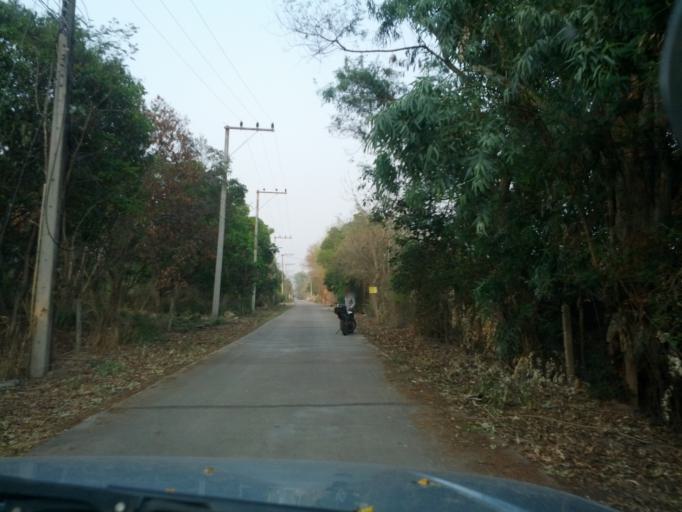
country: TH
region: Chiang Mai
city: San Sai
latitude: 18.9277
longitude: 99.0125
